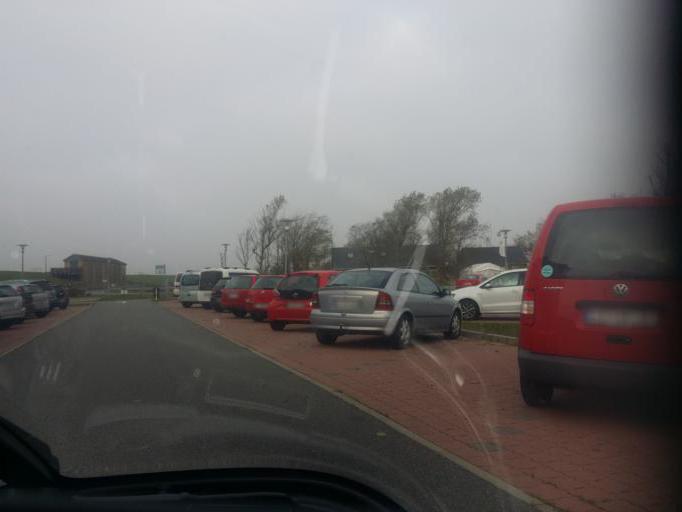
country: DE
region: Schleswig-Holstein
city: Grode
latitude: 54.6811
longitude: 8.7572
